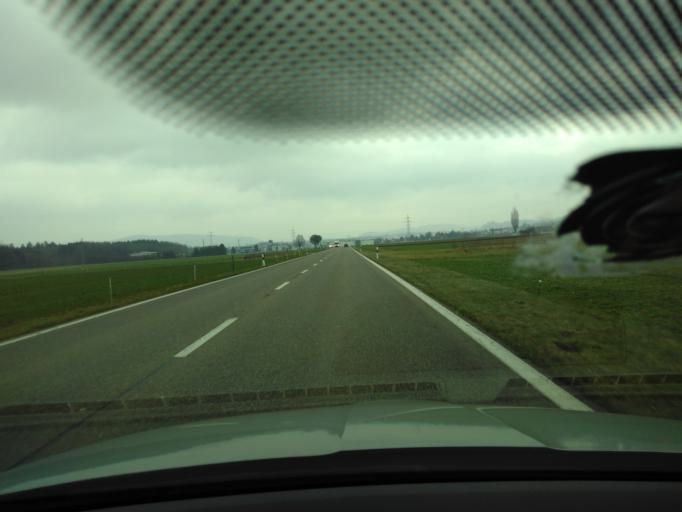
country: CH
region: Aargau
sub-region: Bezirk Aarau
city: Buchs
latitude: 47.3835
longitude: 8.1019
